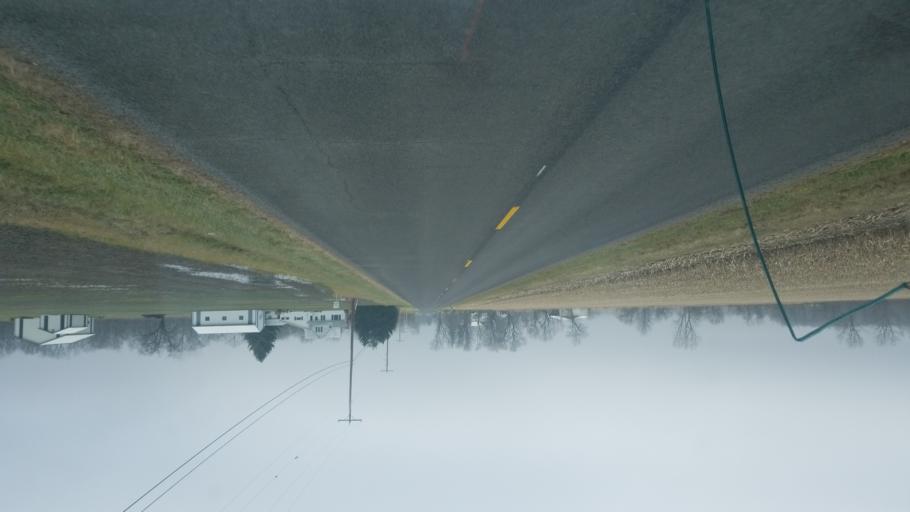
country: US
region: Ohio
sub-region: Champaign County
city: North Lewisburg
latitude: 40.3356
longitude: -83.5729
